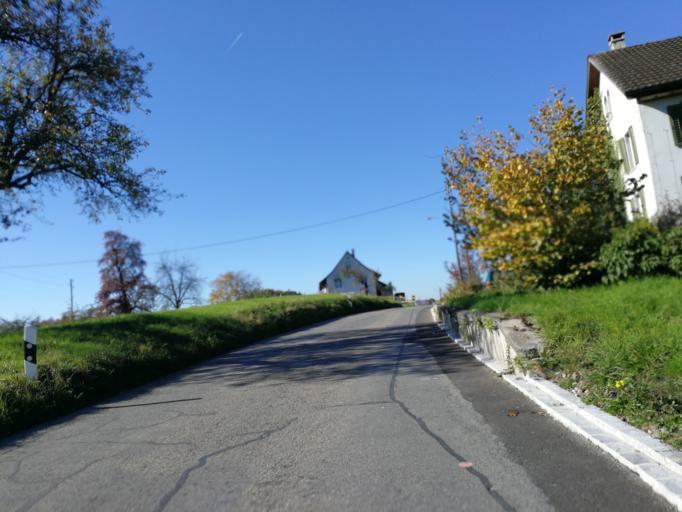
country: CH
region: Zurich
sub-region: Bezirk Hinwil
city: Binzikon
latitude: 47.2641
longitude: 8.7583
